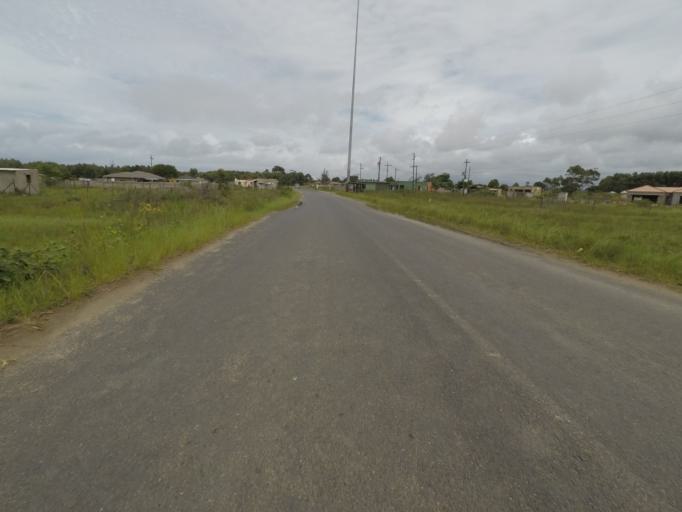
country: ZA
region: KwaZulu-Natal
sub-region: uThungulu District Municipality
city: eSikhawini
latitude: -28.9111
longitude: 31.8650
